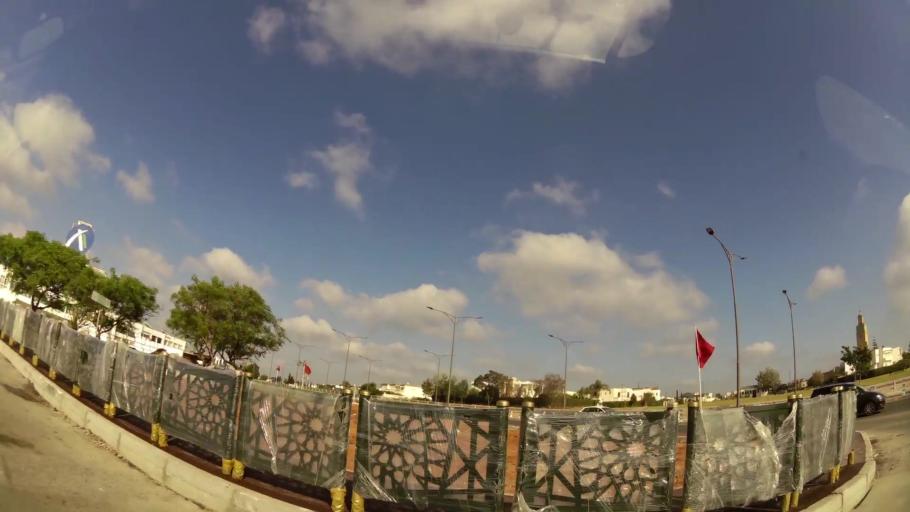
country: MA
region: Rabat-Sale-Zemmour-Zaer
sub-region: Skhirate-Temara
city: Temara
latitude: 33.9477
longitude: -6.8706
